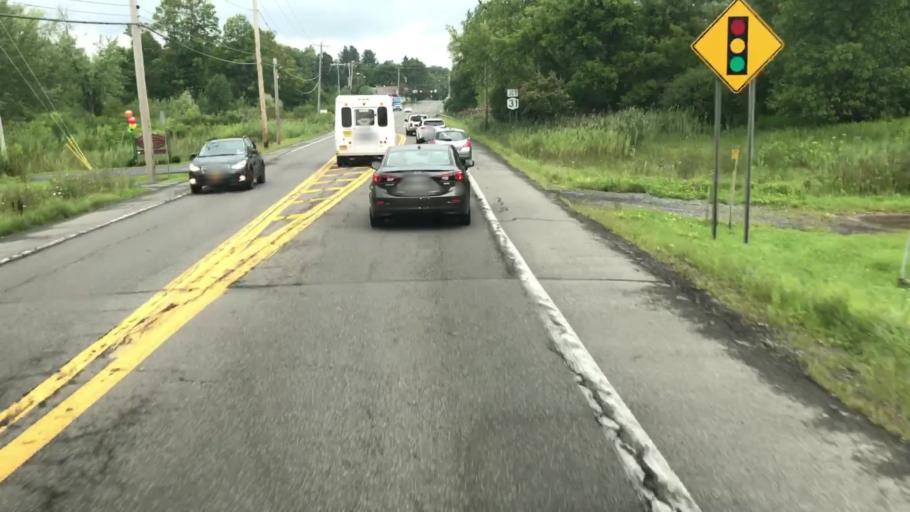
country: US
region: New York
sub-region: Onondaga County
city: Liverpool
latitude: 43.1837
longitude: -76.2167
